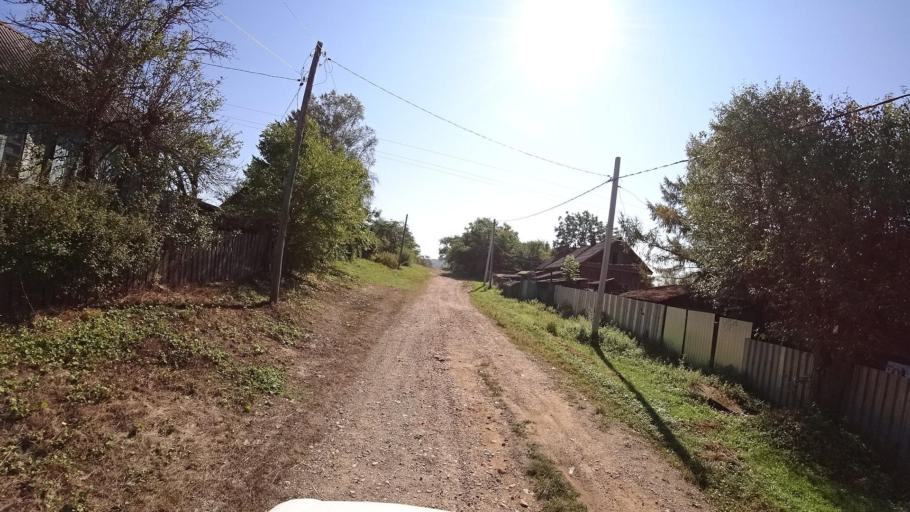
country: RU
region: Jewish Autonomous Oblast
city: Bira
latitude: 49.0053
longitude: 132.4678
